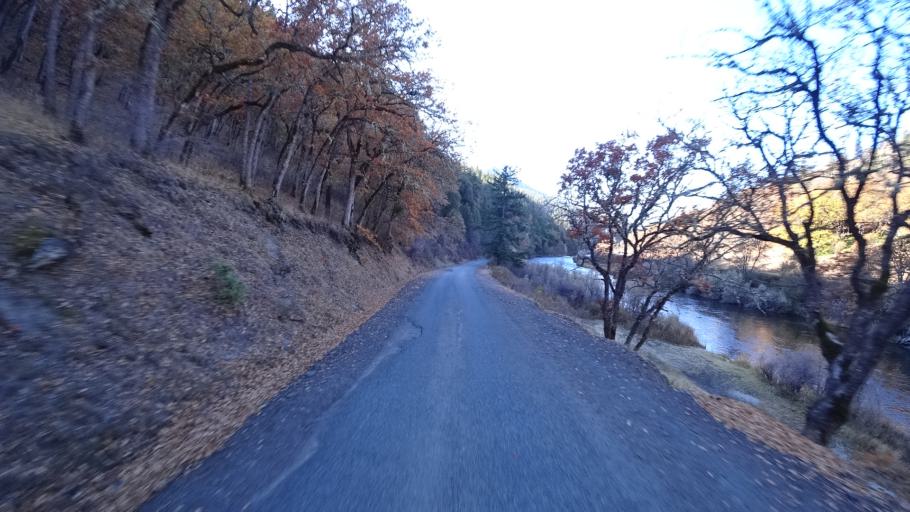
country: US
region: California
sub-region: Siskiyou County
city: Yreka
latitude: 41.8449
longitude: -122.9073
